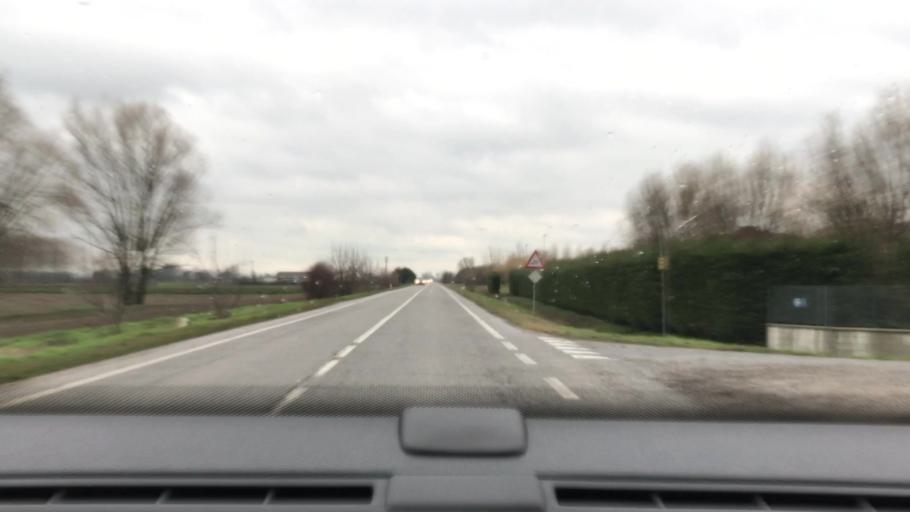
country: IT
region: Lombardy
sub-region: Provincia di Cremona
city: Torricella del Pizzo
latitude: 45.0332
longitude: 10.3036
